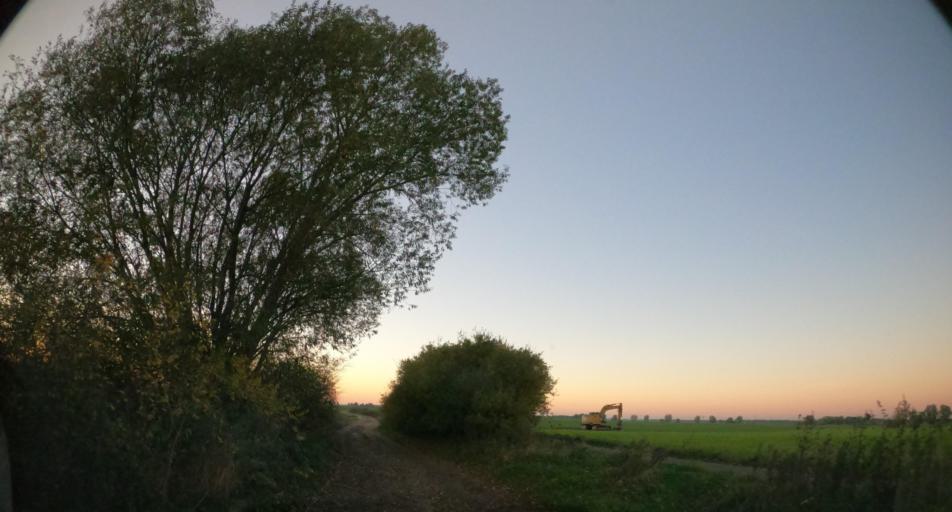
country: DE
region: Mecklenburg-Vorpommern
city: Ducherow
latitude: 53.7796
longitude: 13.8544
